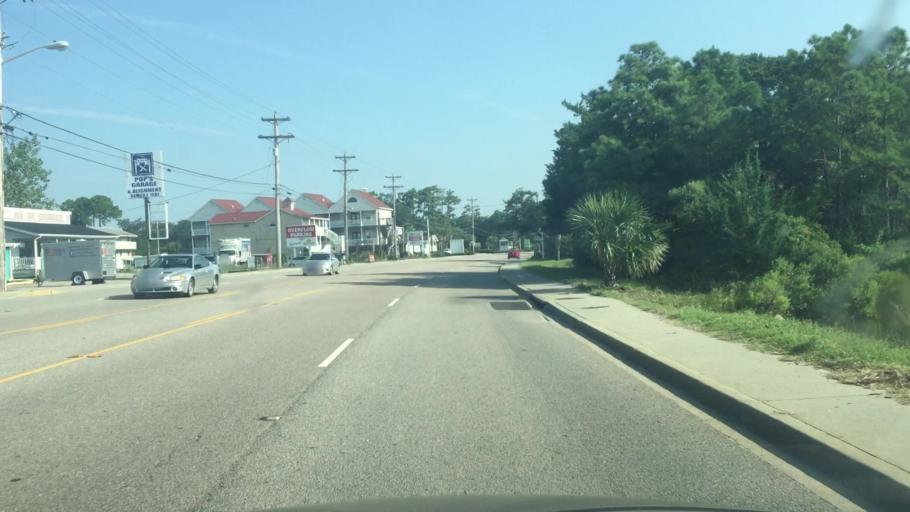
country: US
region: South Carolina
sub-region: Horry County
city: North Myrtle Beach
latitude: 33.8326
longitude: -78.6446
